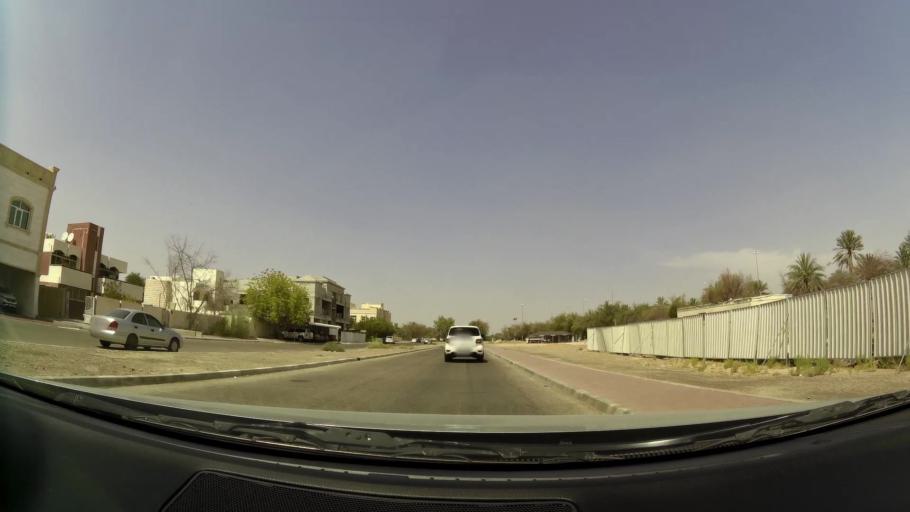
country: AE
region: Abu Dhabi
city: Al Ain
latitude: 24.2217
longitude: 55.6946
